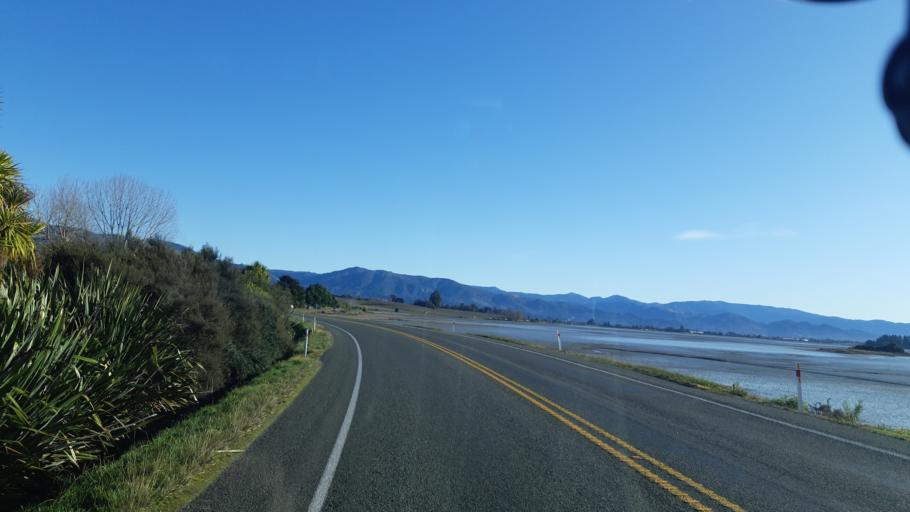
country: NZ
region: Tasman
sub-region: Tasman District
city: Motueka
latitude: -41.1639
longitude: 173.0274
